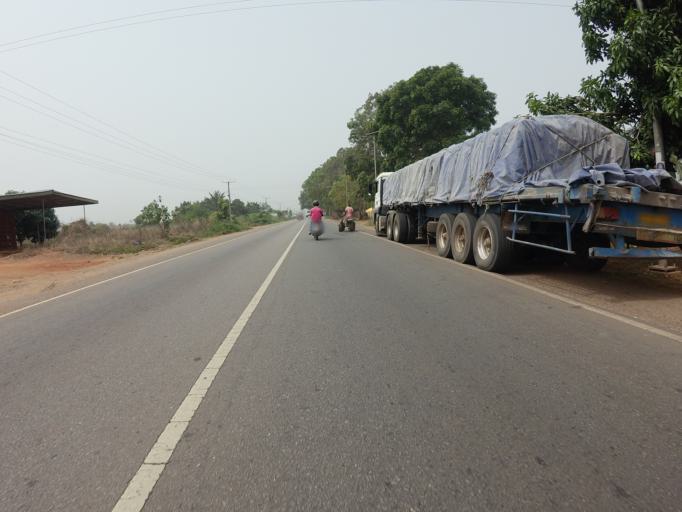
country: GH
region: Volta
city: Anloga
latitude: 5.8957
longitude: 0.5131
